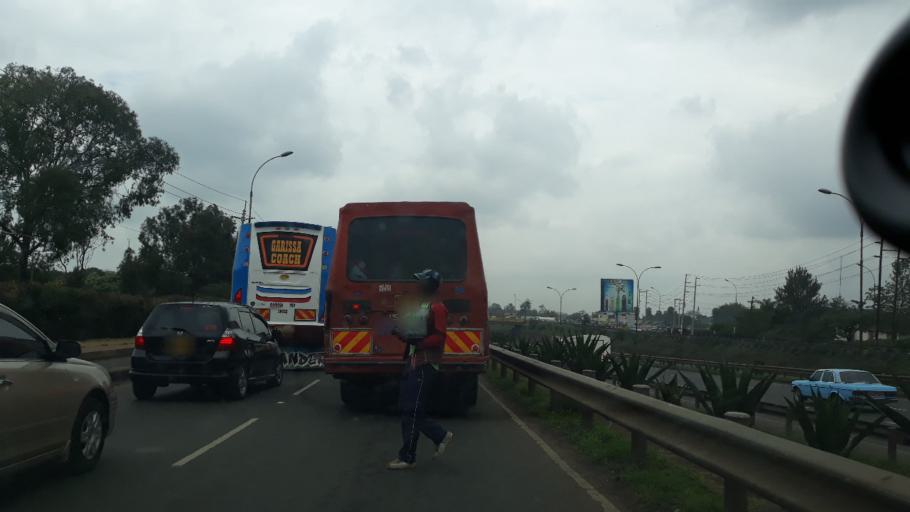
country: KE
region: Nairobi Area
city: Pumwani
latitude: -1.2465
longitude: 36.8650
